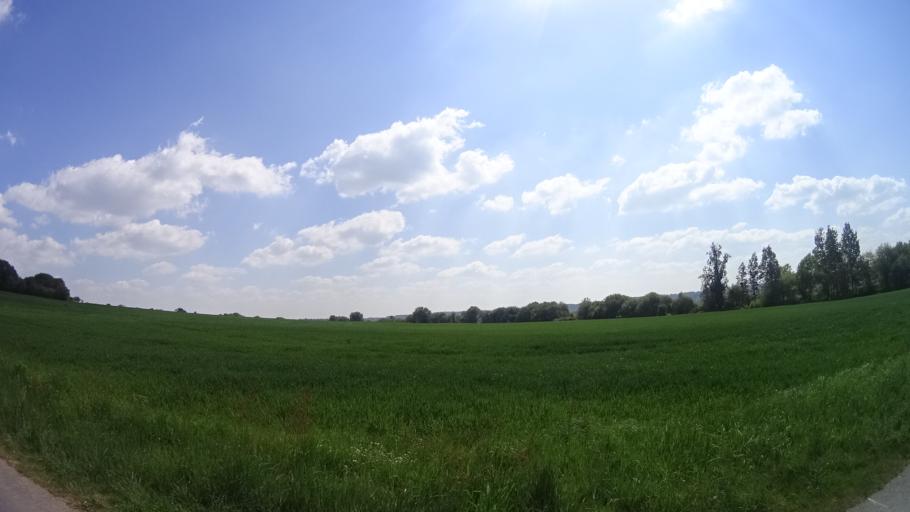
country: FR
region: Brittany
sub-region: Departement du Morbihan
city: Allaire
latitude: 47.5999
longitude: -2.1900
